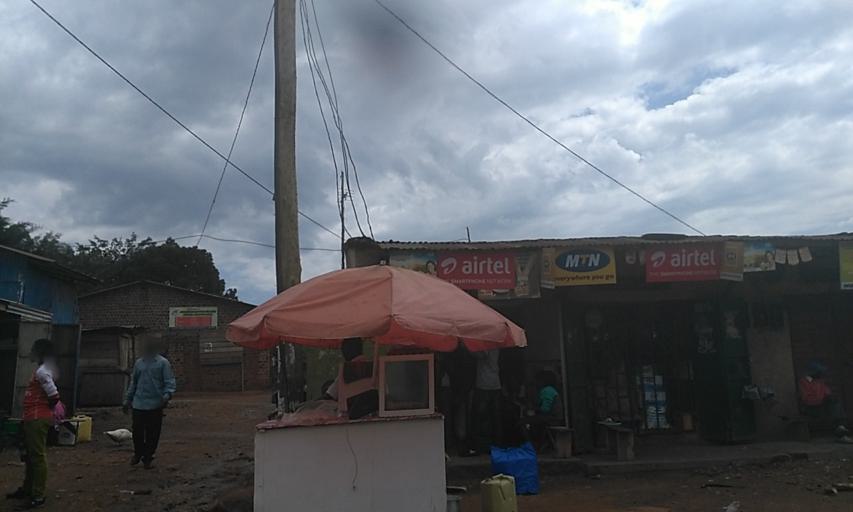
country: UG
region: Central Region
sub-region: Wakiso District
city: Kireka
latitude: 0.3669
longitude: 32.6485
